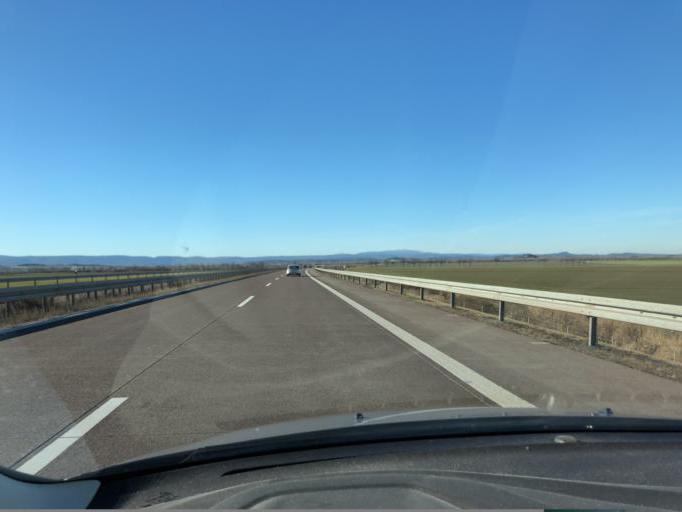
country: DE
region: Saxony-Anhalt
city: Gatersleben
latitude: 51.8015
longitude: 11.2432
